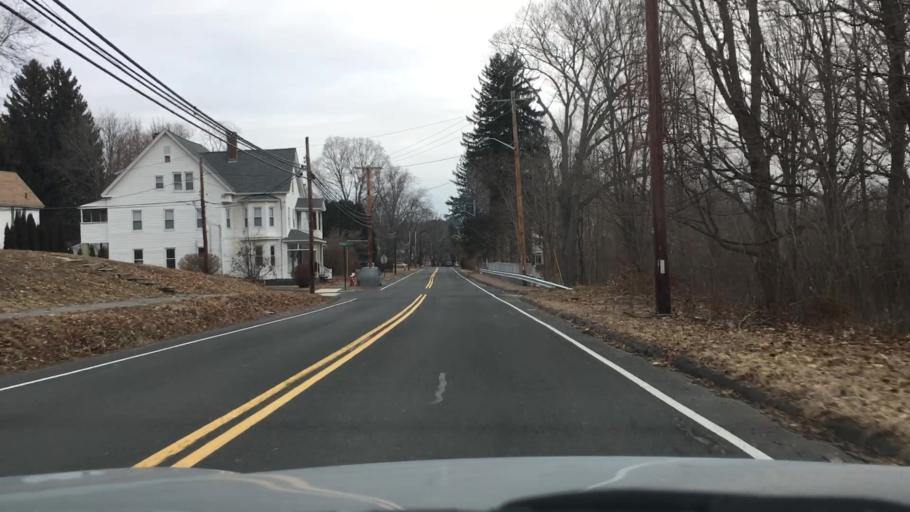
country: US
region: Massachusetts
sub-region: Hampshire County
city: Northampton
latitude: 42.3224
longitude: -72.6605
